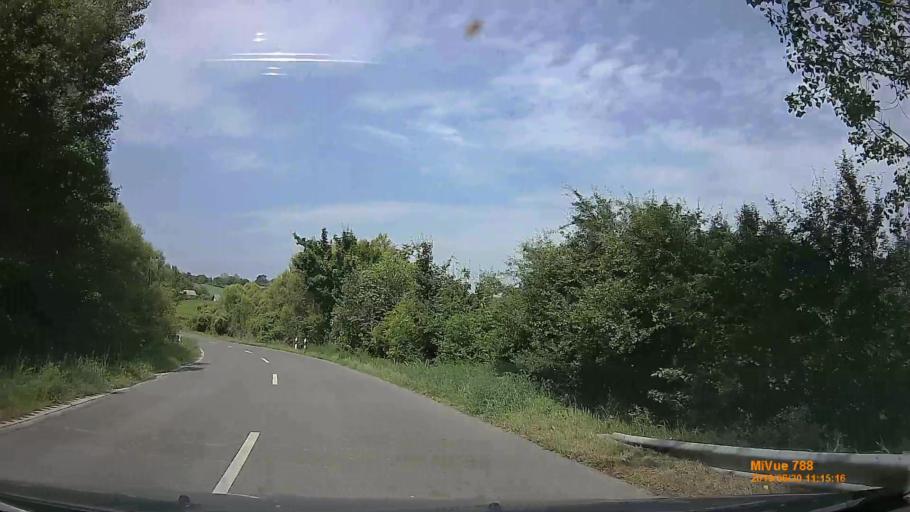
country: HU
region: Baranya
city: Pecsvarad
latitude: 46.1505
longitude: 18.4902
